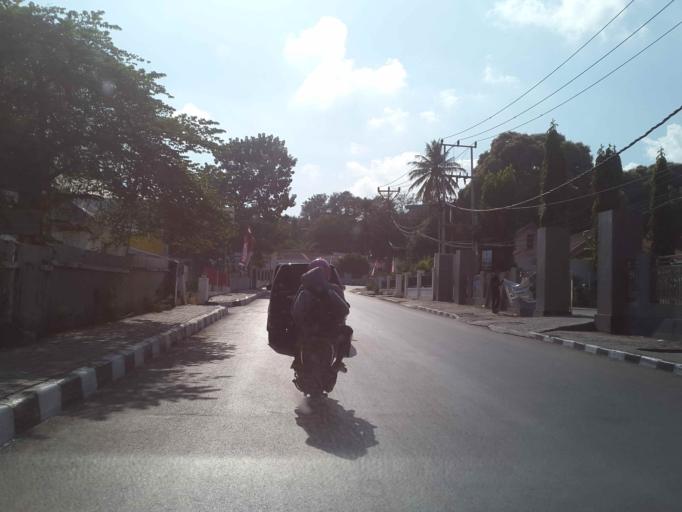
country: ID
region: East Nusa Tenggara
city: Lai Lai Bisi Kopan
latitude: -10.1642
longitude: 123.5785
